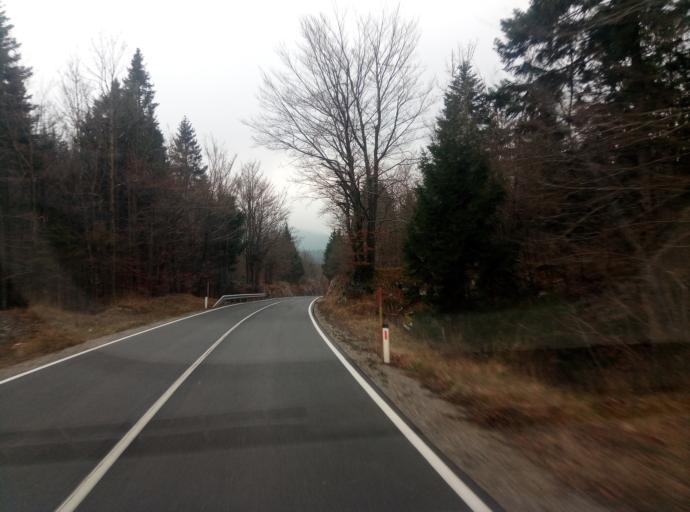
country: SI
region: Idrija
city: Idrija
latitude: 45.9389
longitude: 14.0726
